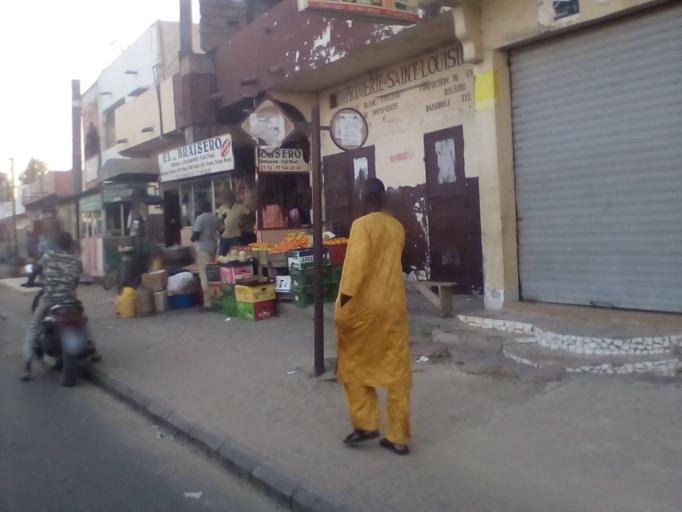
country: SN
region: Saint-Louis
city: Saint-Louis
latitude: 16.0206
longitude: -16.4911
